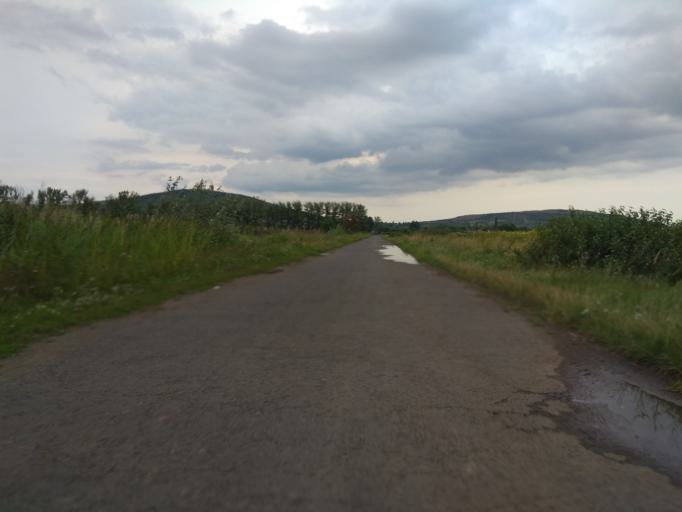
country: HU
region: Borsod-Abauj-Zemplen
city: Bekecs
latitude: 48.1570
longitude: 21.1327
